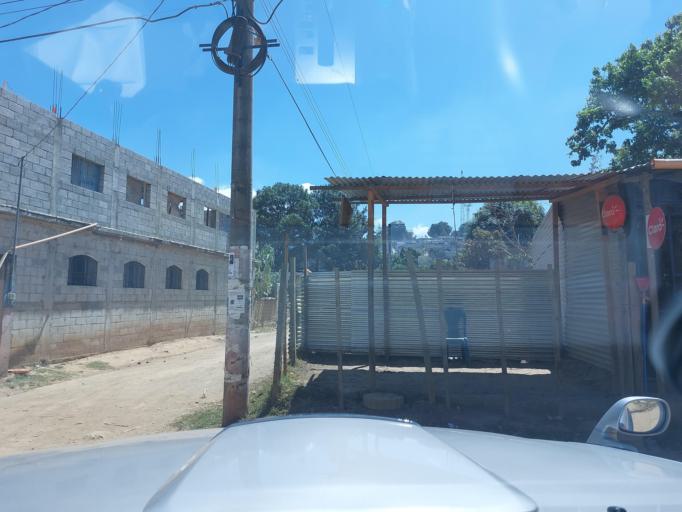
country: GT
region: Chimaltenango
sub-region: Municipio de Chimaltenango
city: Chimaltenango
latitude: 14.6533
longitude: -90.8259
